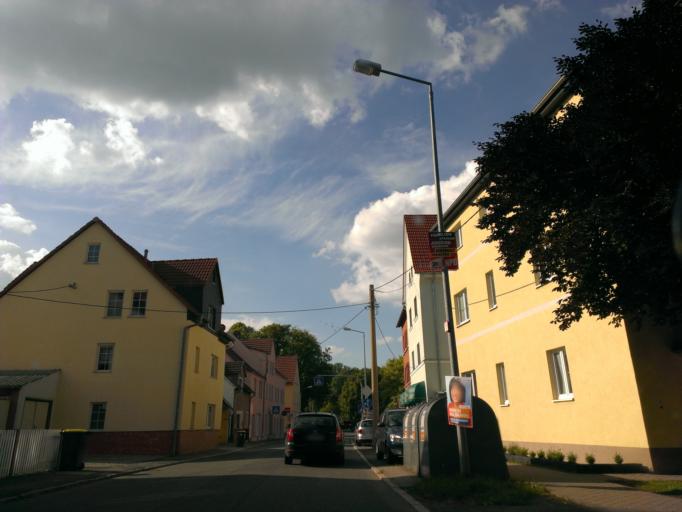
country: DE
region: Thuringia
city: Erfurt
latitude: 50.9550
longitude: 11.0009
